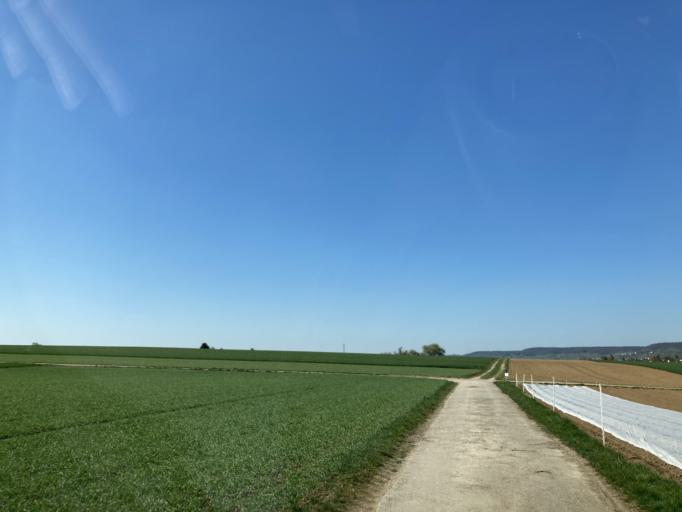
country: DE
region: Baden-Wuerttemberg
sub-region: Tuebingen Region
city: Rottenburg
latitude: 48.5345
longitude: 8.9236
